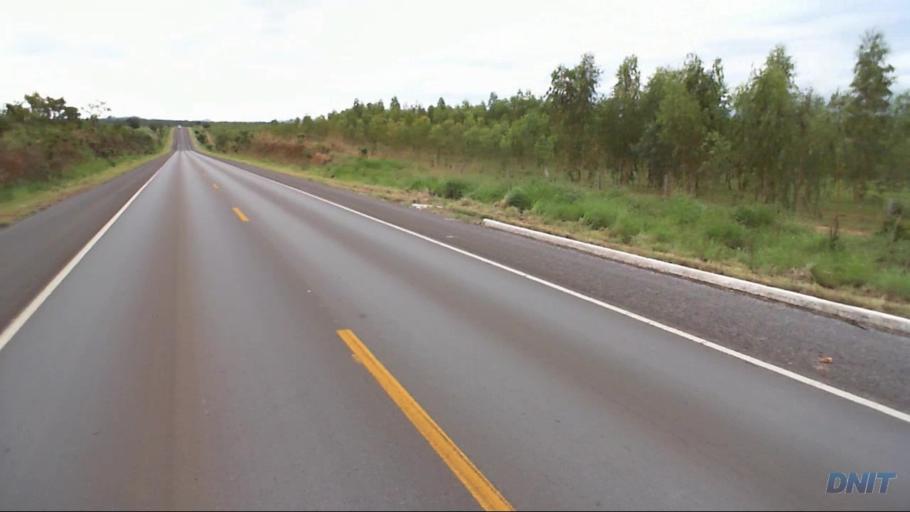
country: BR
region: Goias
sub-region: Barro Alto
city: Barro Alto
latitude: -15.2162
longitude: -48.6553
